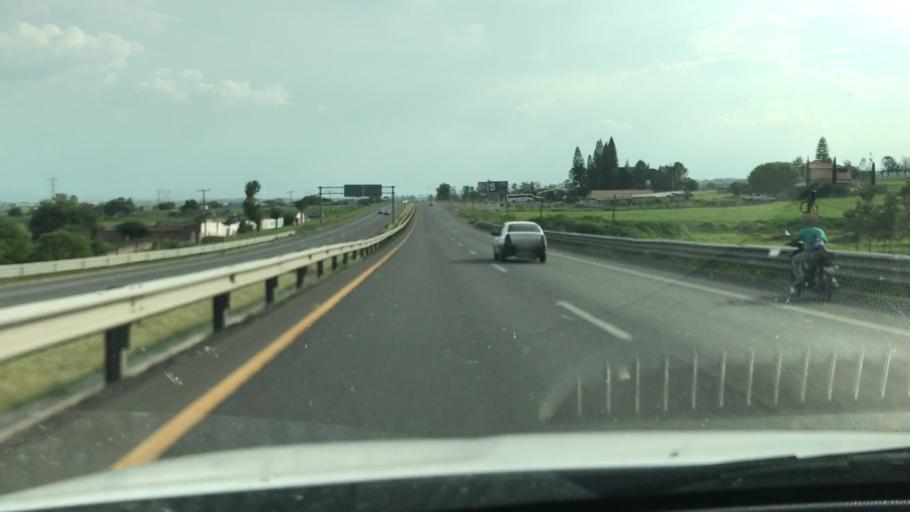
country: MX
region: Guanajuato
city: Penjamo
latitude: 20.4139
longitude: -101.7321
